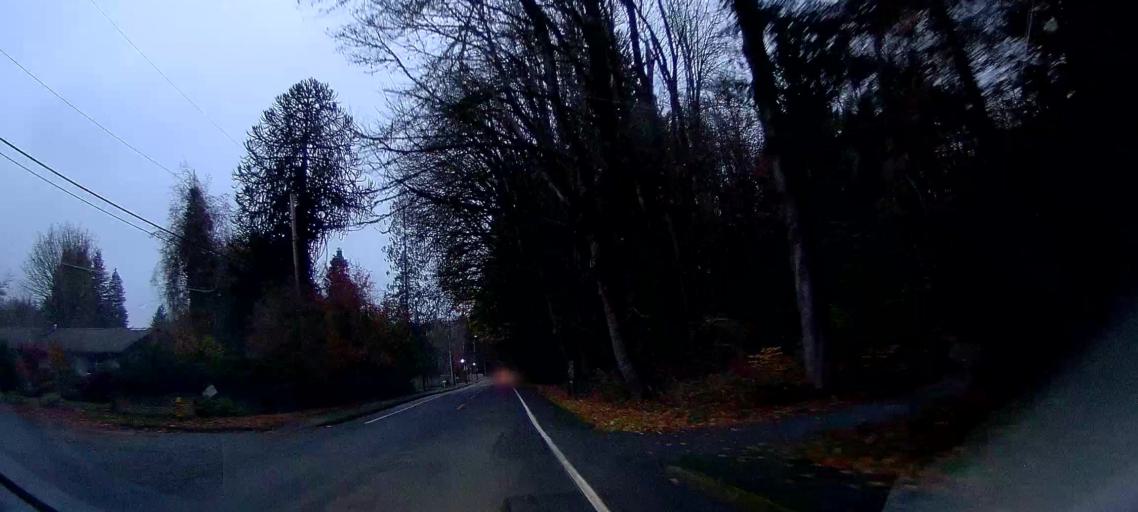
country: US
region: Washington
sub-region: Thurston County
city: Olympia
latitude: 47.0274
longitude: -122.8737
